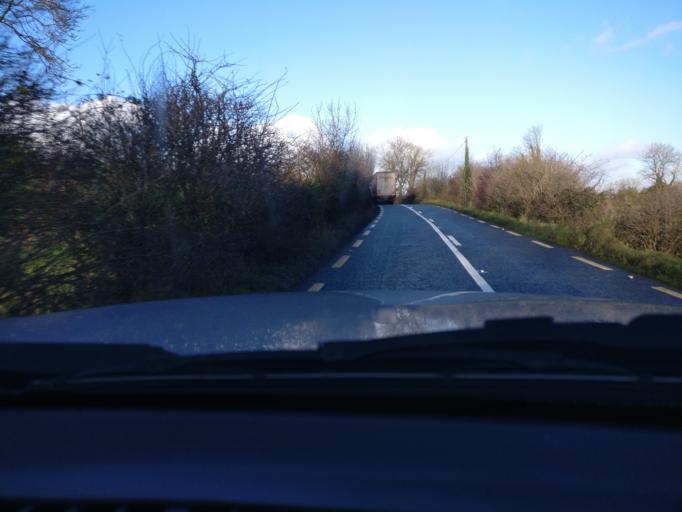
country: IE
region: Leinster
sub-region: An Mhi
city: Athboy
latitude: 53.6556
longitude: -7.0262
